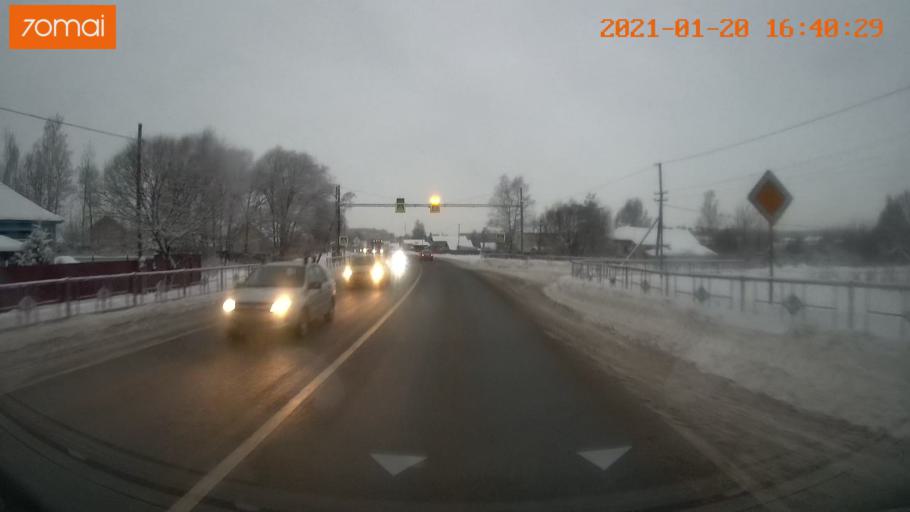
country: RU
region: Vladimir
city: Orgtrud
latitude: 56.2095
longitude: 40.6673
